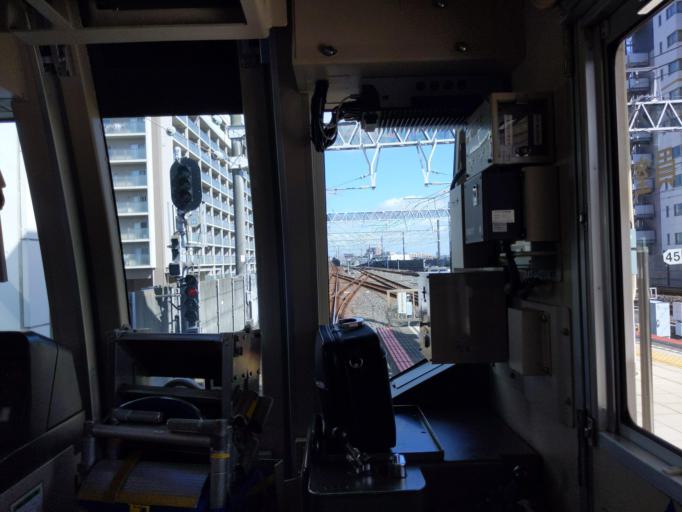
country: JP
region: Chiba
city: Shiroi
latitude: 35.7291
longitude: 140.0742
